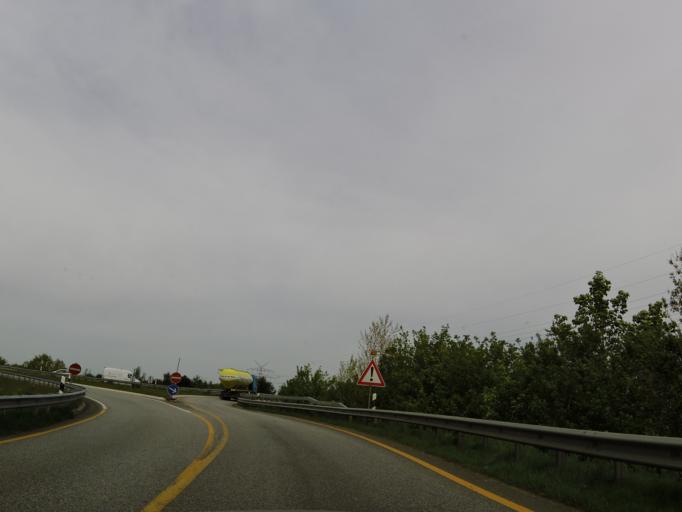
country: DE
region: Schleswig-Holstein
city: Heiligenstedten
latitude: 53.9344
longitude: 9.4842
